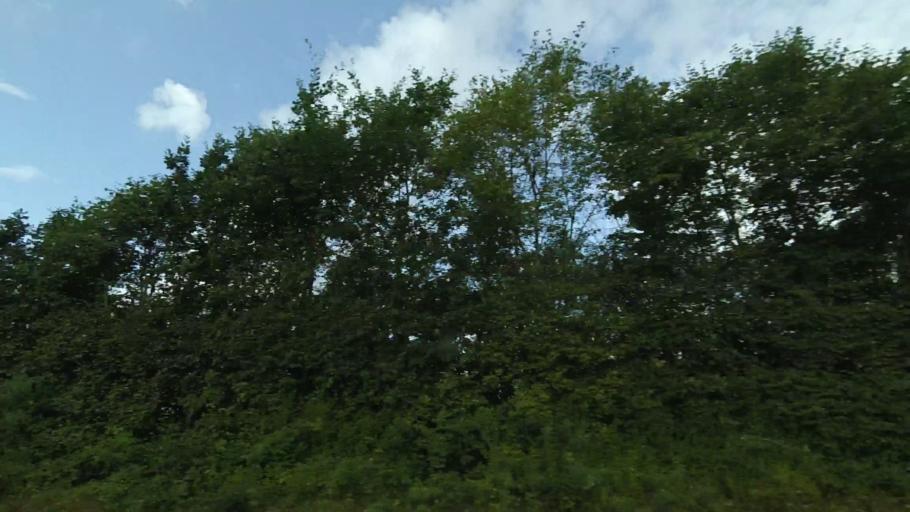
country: DK
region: Central Jutland
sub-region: Syddjurs Kommune
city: Ryomgard
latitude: 56.4250
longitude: 10.5573
